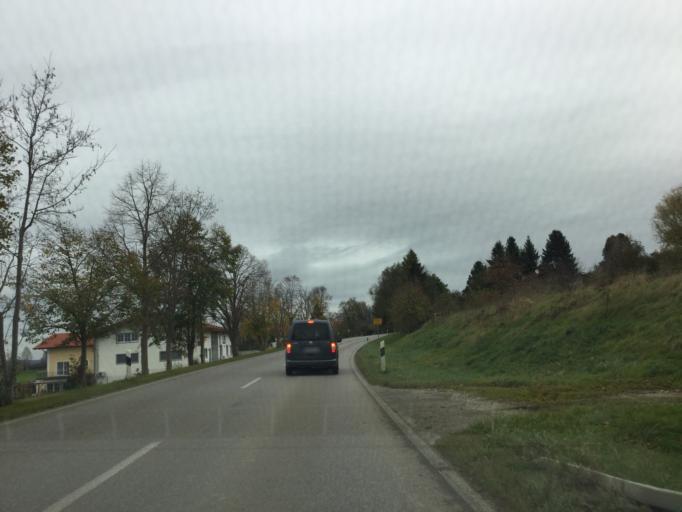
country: DE
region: Bavaria
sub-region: Upper Bavaria
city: Pahl
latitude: 47.9236
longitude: 11.1576
